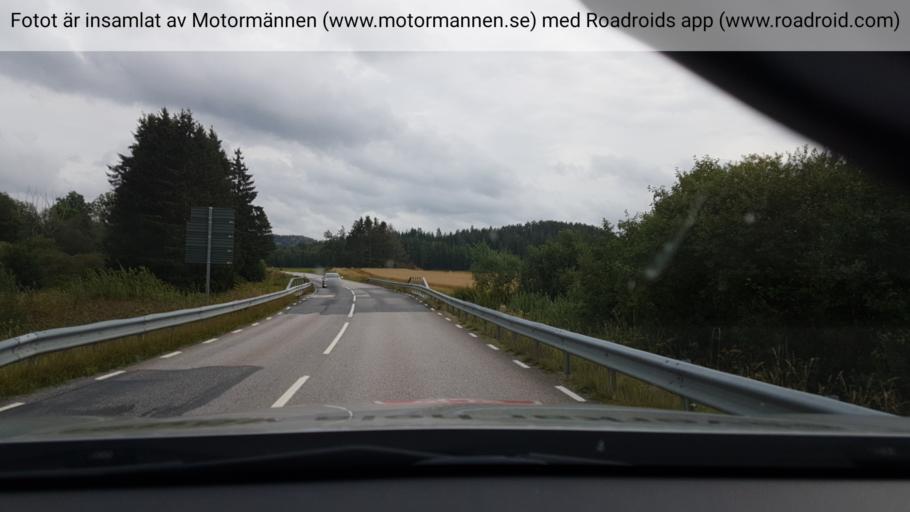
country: SE
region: Vaestra Goetaland
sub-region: Sotenas Kommun
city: Hunnebostrand
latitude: 58.5561
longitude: 11.4028
